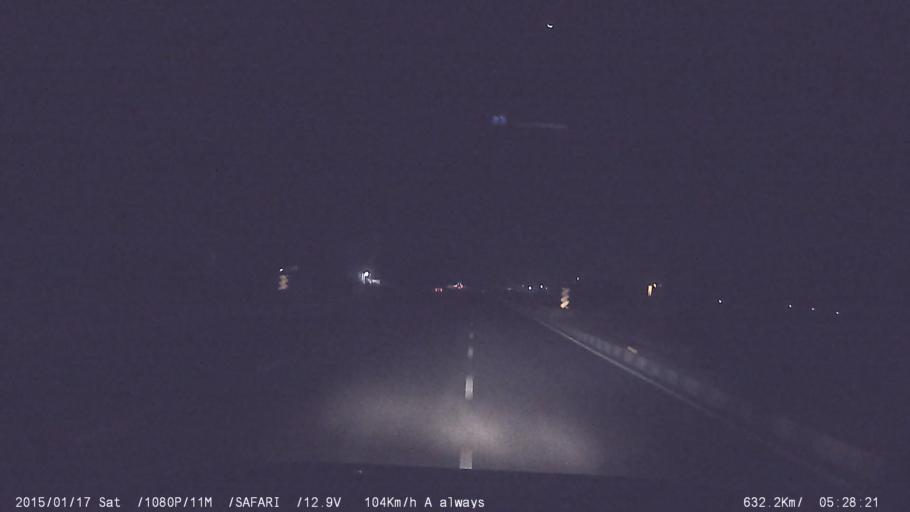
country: IN
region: Tamil Nadu
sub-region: Vellore
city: Arcot
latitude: 12.9259
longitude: 79.2709
